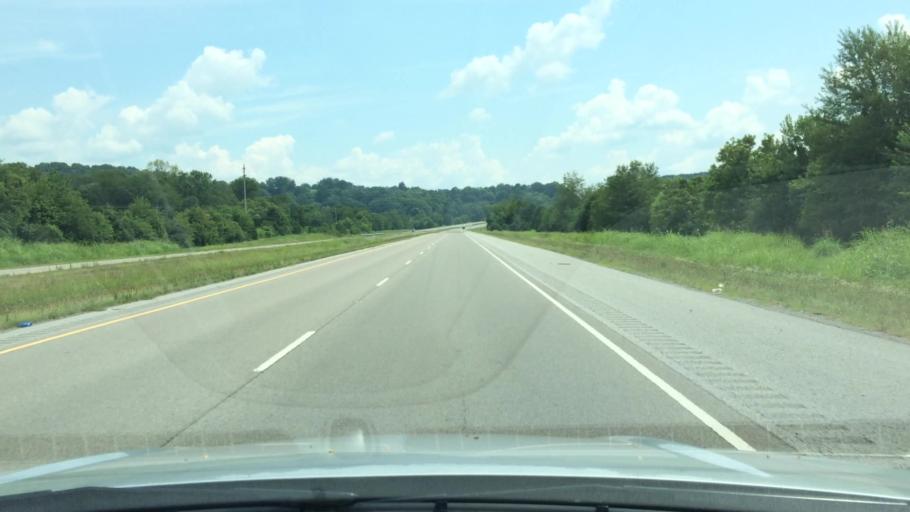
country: US
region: Tennessee
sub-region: Giles County
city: Pulaski
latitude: 35.1728
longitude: -87.0050
